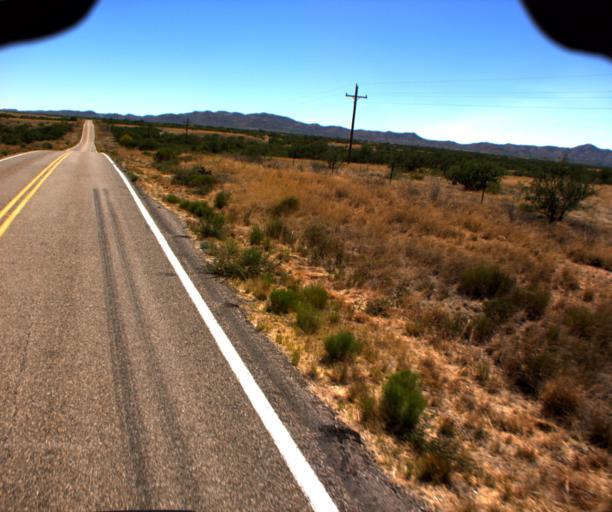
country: US
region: Arizona
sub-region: Pima County
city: Sells
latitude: 31.5955
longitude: -111.5279
